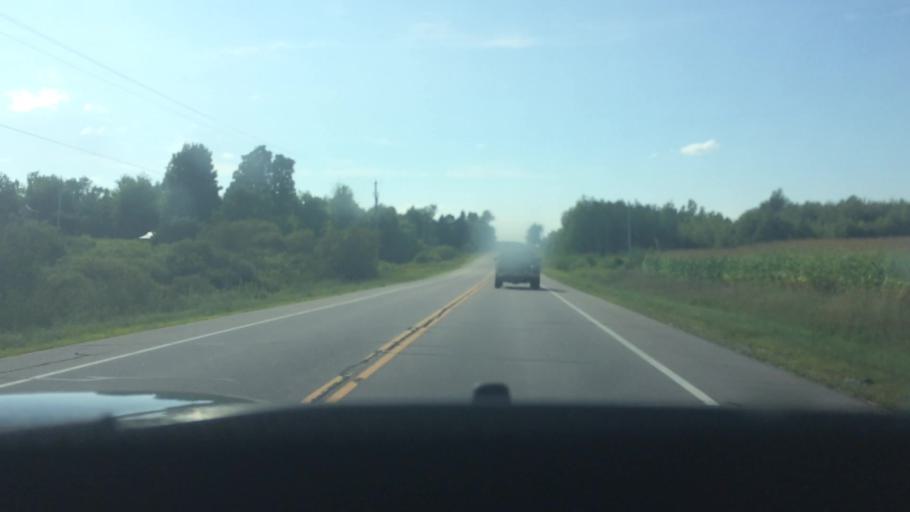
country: US
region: New York
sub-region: Franklin County
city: Malone
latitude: 44.8519
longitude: -74.2087
